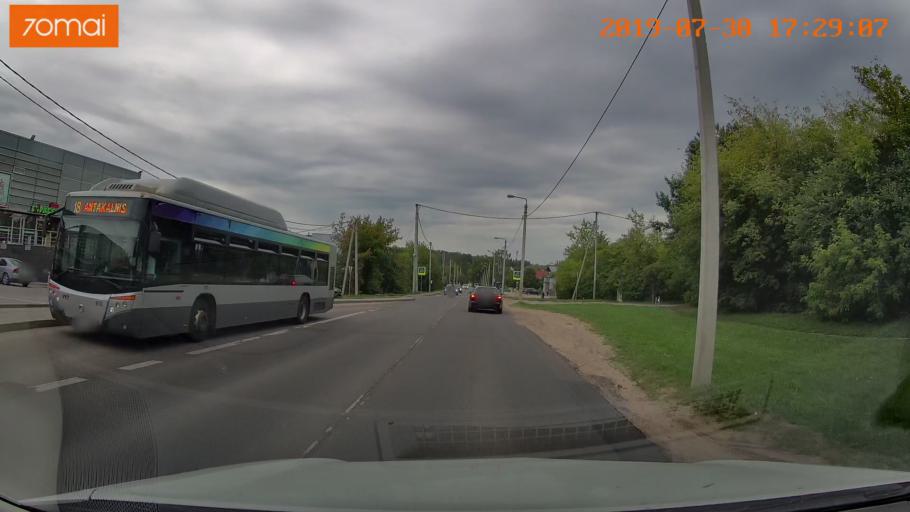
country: LT
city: Skaidiskes
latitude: 54.7012
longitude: 25.4107
